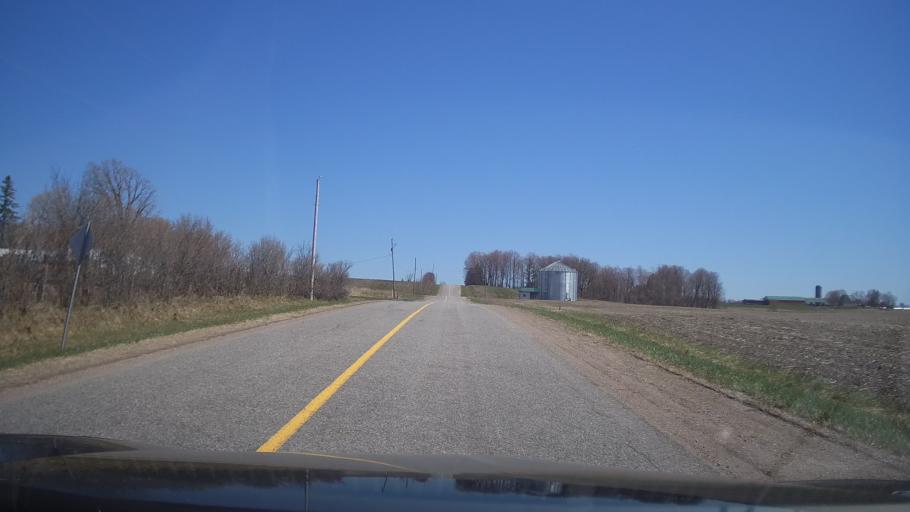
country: CA
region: Ontario
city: Arnprior
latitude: 45.5324
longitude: -76.3945
